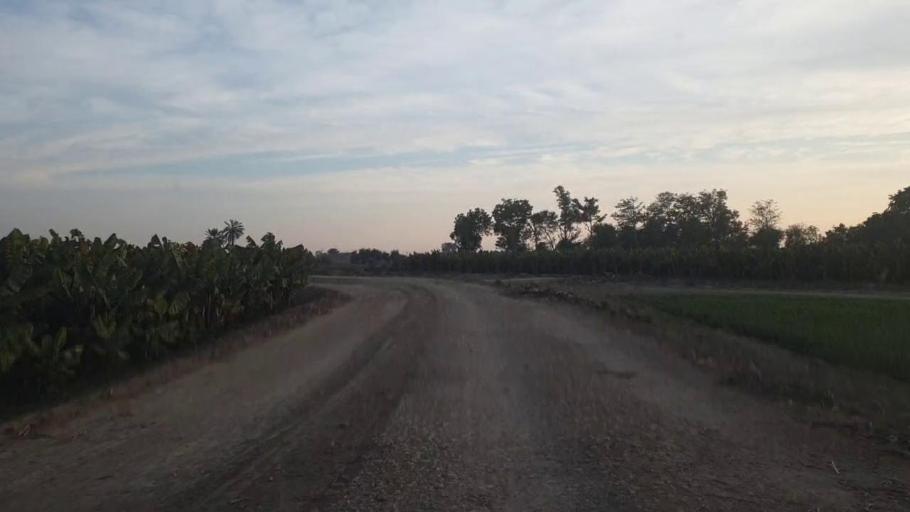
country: PK
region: Sindh
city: Shahdadpur
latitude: 26.0507
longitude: 68.5323
